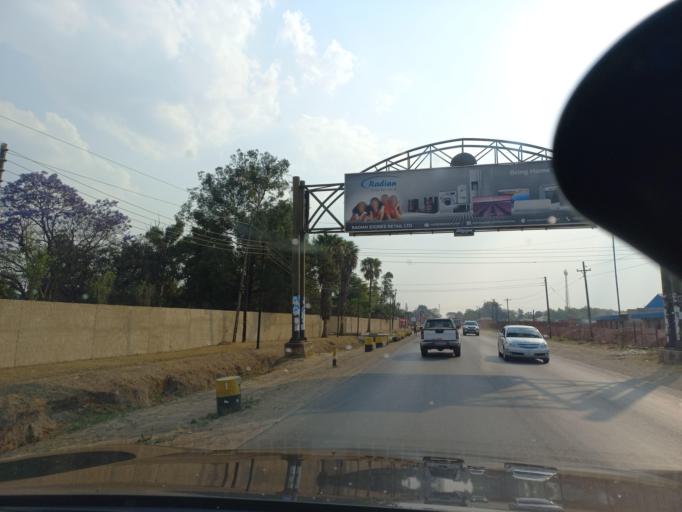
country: ZM
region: Lusaka
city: Lusaka
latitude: -15.4572
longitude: 28.2606
